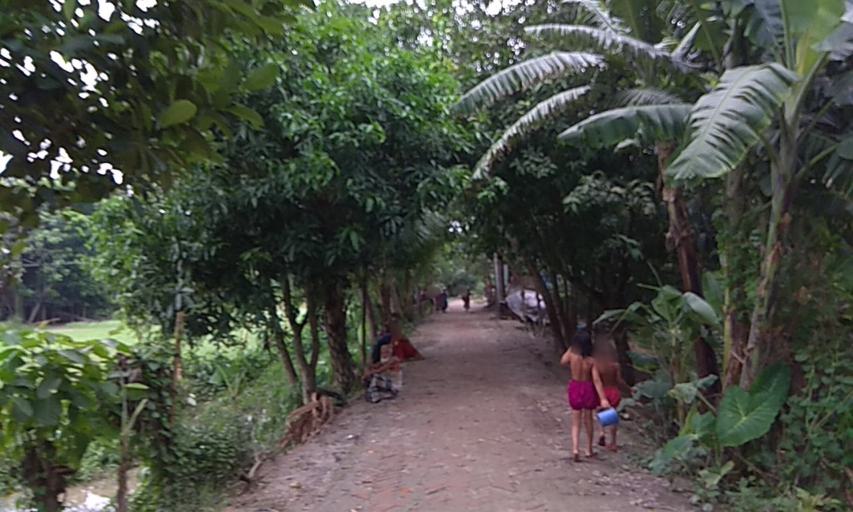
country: BD
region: Dhaka
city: Dohar
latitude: 23.5420
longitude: 89.9921
